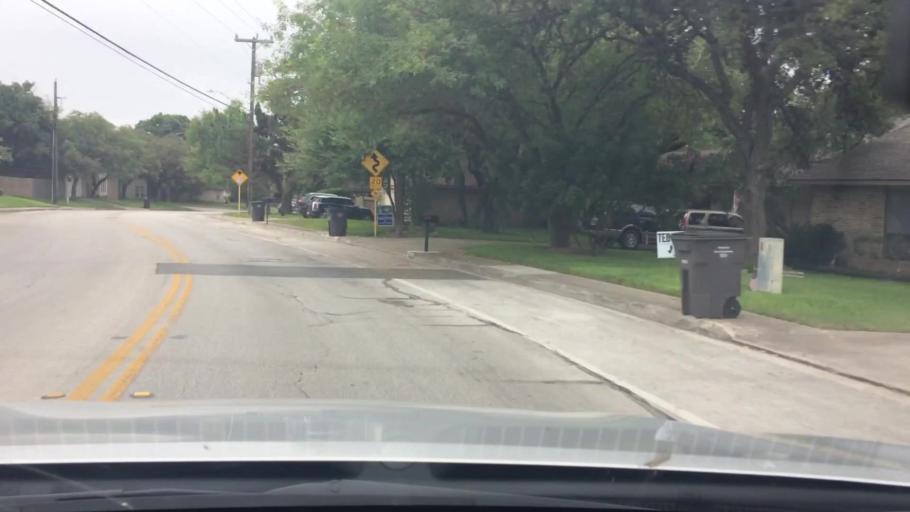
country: US
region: Texas
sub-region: Bexar County
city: Hollywood Park
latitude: 29.5813
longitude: -98.4560
